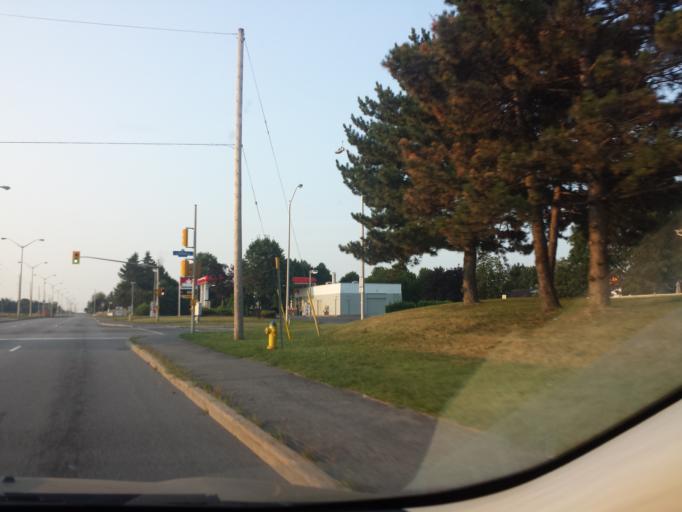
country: CA
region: Ontario
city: Bells Corners
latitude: 45.3109
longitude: -75.8807
